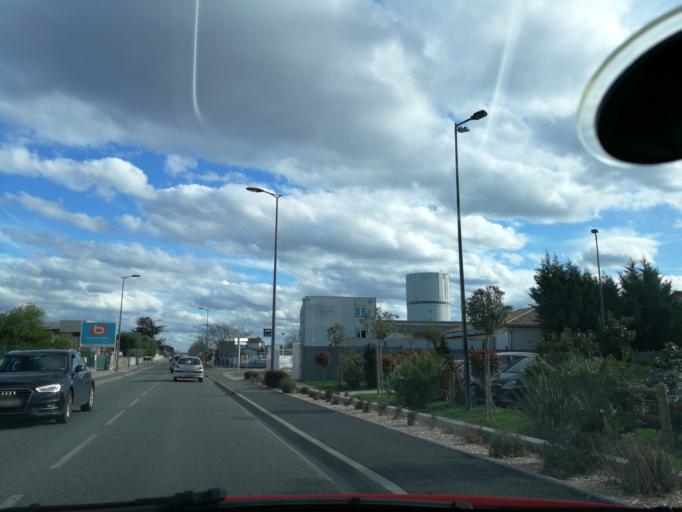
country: FR
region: Midi-Pyrenees
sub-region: Departement de la Haute-Garonne
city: Blagnac
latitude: 43.6480
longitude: 1.3831
